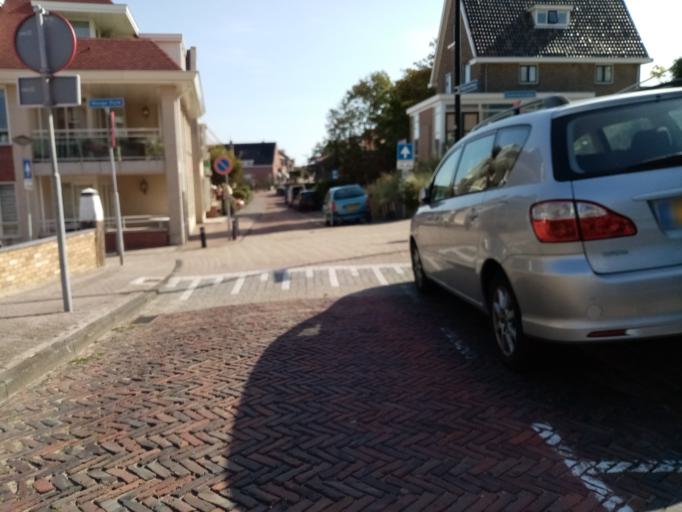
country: NL
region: South Holland
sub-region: Gemeente Noordwijk
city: Noordwijk-Binnen
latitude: 52.2415
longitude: 4.4338
